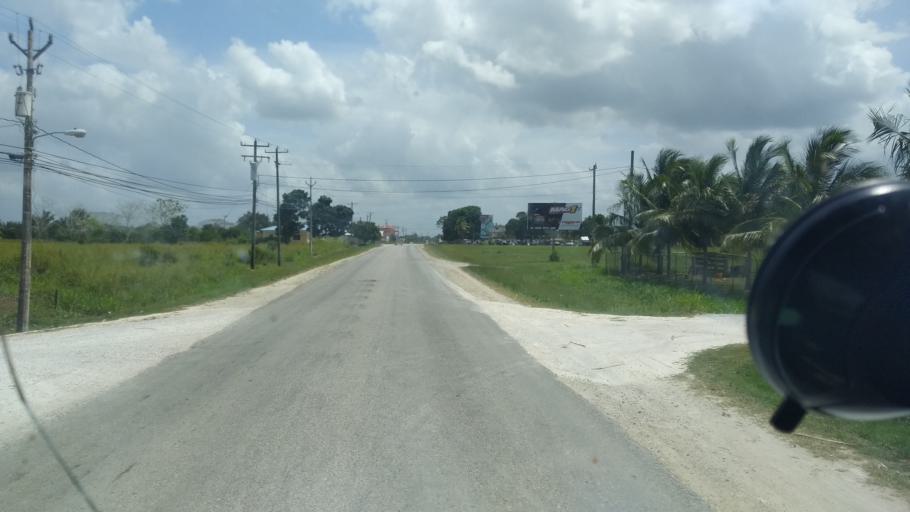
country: BZ
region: Orange Walk
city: Orange Walk
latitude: 18.0607
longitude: -88.5708
